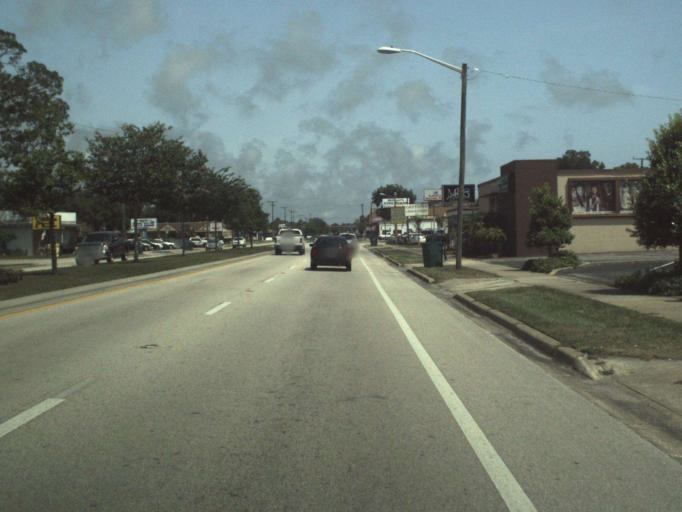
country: US
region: Florida
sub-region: Volusia County
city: Holly Hill
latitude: 29.2570
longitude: -81.0475
